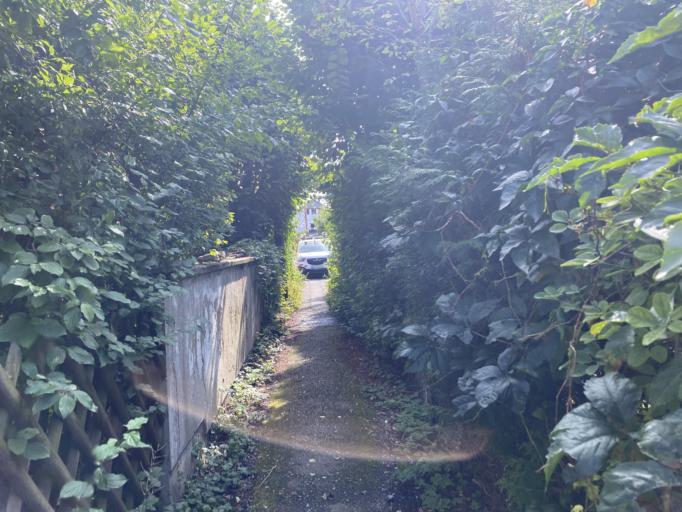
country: DE
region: Bavaria
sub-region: Upper Bavaria
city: Olching
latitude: 48.2004
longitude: 11.3106
